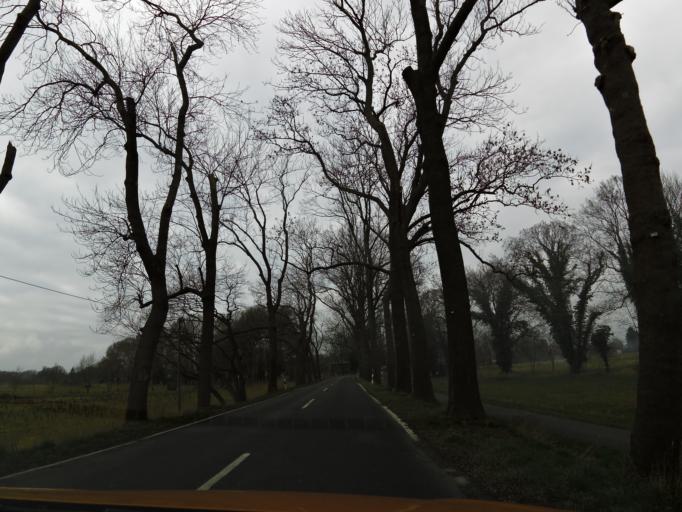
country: DE
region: Brandenburg
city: Ketzin
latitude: 52.4682
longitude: 12.8820
